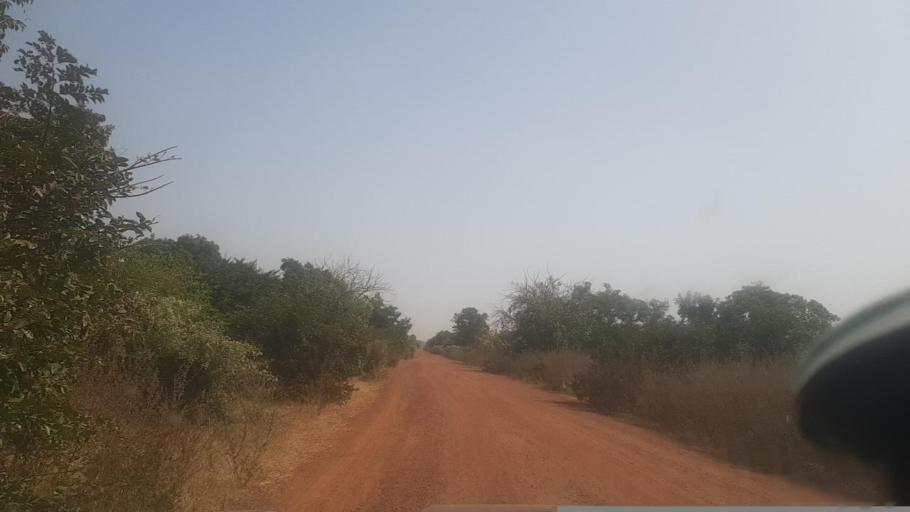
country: ML
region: Segou
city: Bla
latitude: 12.9193
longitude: -6.2567
